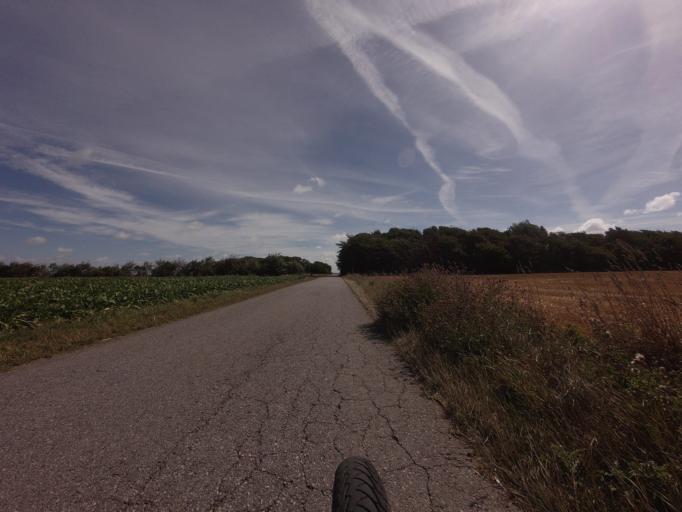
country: DK
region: North Denmark
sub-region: Jammerbugt Kommune
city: Pandrup
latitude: 57.3428
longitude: 9.7831
